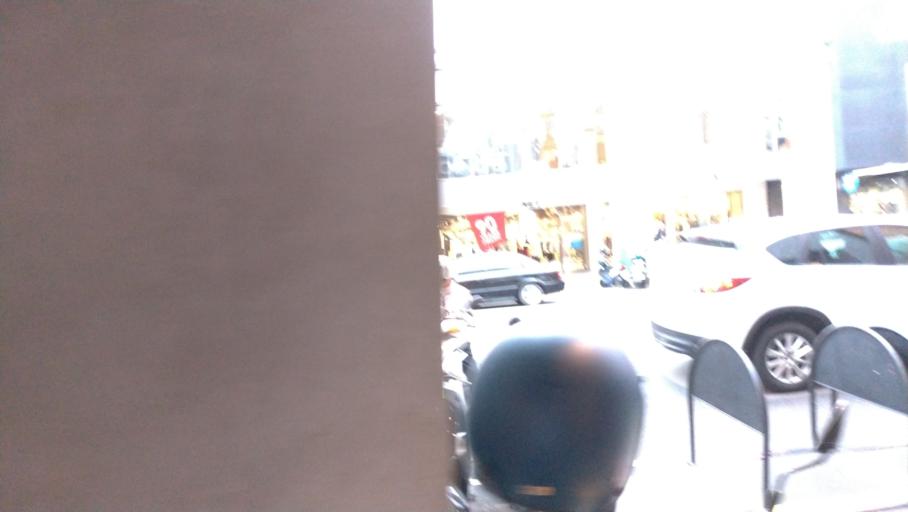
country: TW
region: Taiwan
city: Fengyuan
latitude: 24.2529
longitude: 120.7220
